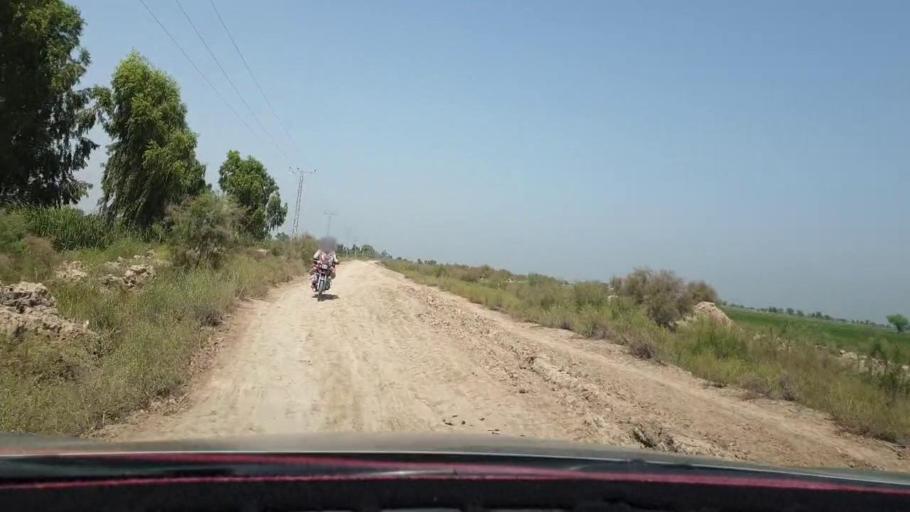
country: PK
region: Sindh
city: Warah
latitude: 27.4173
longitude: 67.6983
